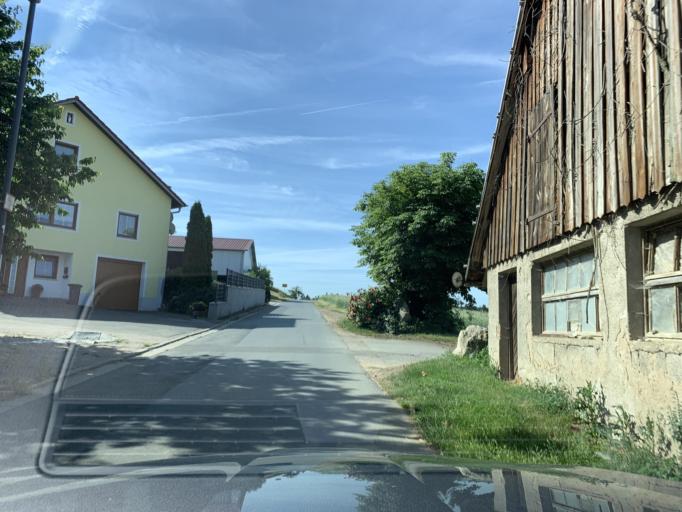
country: DE
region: Bavaria
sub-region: Upper Palatinate
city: Schwarzhofen
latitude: 49.4072
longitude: 12.3396
